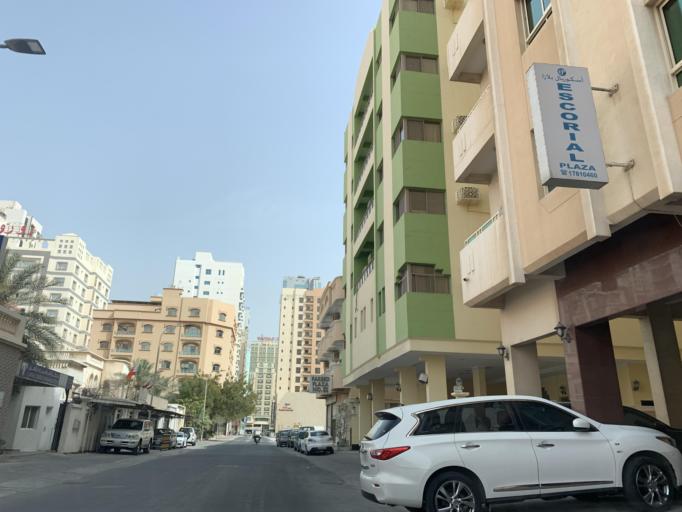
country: BH
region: Manama
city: Manama
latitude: 26.2179
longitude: 50.6087
